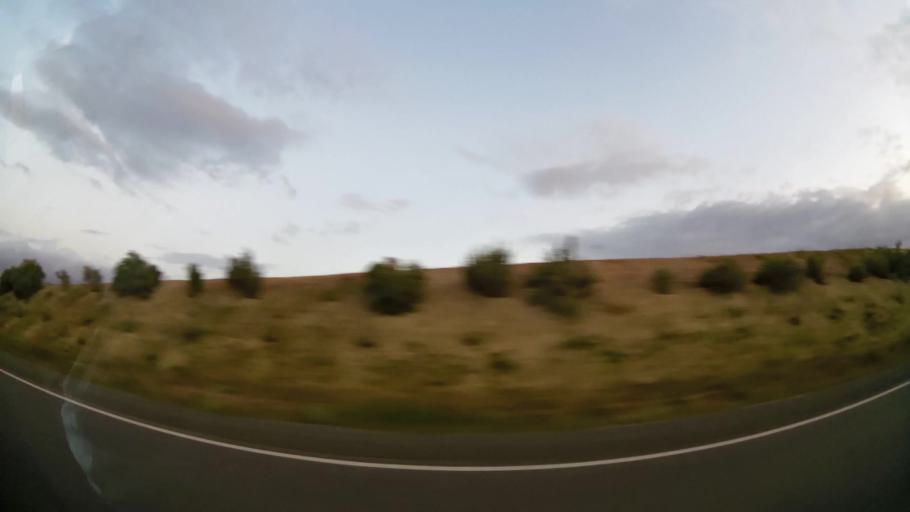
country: MA
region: Oriental
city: El Aioun
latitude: 34.6260
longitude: -2.5119
